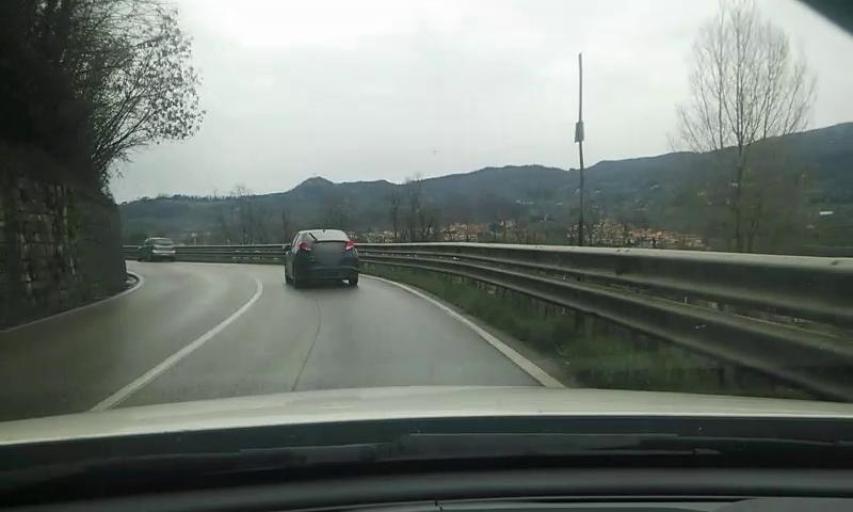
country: IT
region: Tuscany
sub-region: Provincia di Prato
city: Vaiano
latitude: 43.9519
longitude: 11.1274
